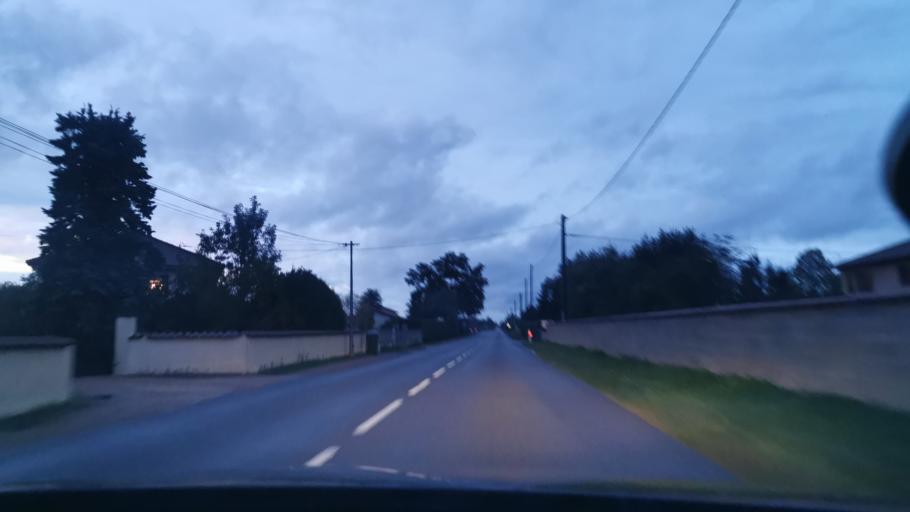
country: FR
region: Rhone-Alpes
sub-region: Departement de l'Ain
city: Bage-la-Ville
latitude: 46.3171
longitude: 4.9331
